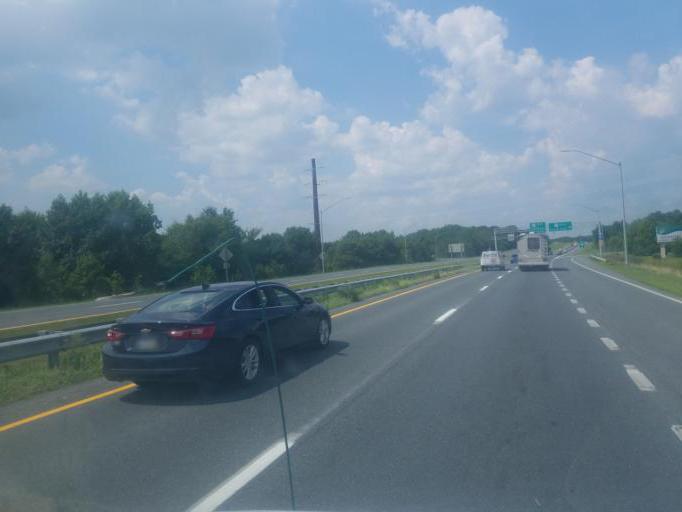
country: US
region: Maryland
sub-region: Worcester County
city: Berlin
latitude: 38.3375
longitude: -75.2119
